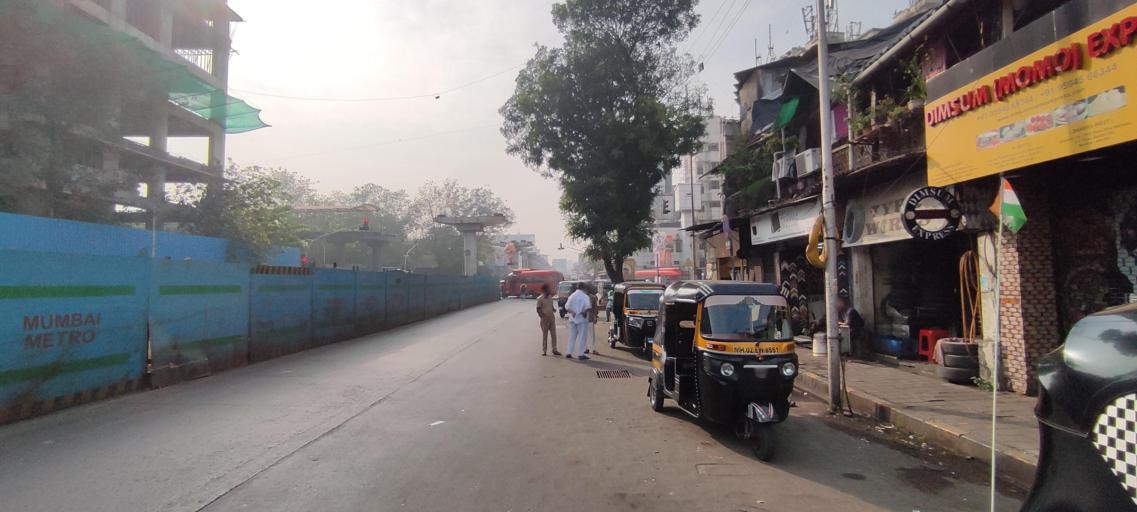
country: IN
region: Maharashtra
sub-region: Mumbai Suburban
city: Mumbai
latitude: 19.0547
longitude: 72.8377
